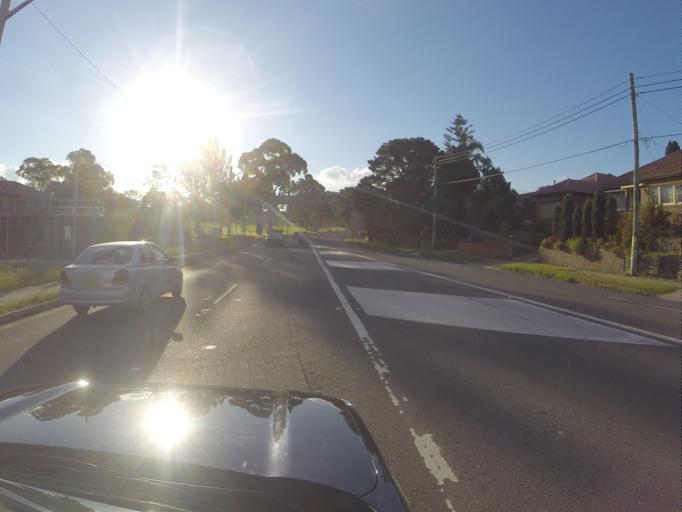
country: AU
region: New South Wales
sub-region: Rockdale
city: Bexley North
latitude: -33.9349
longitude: 151.1108
